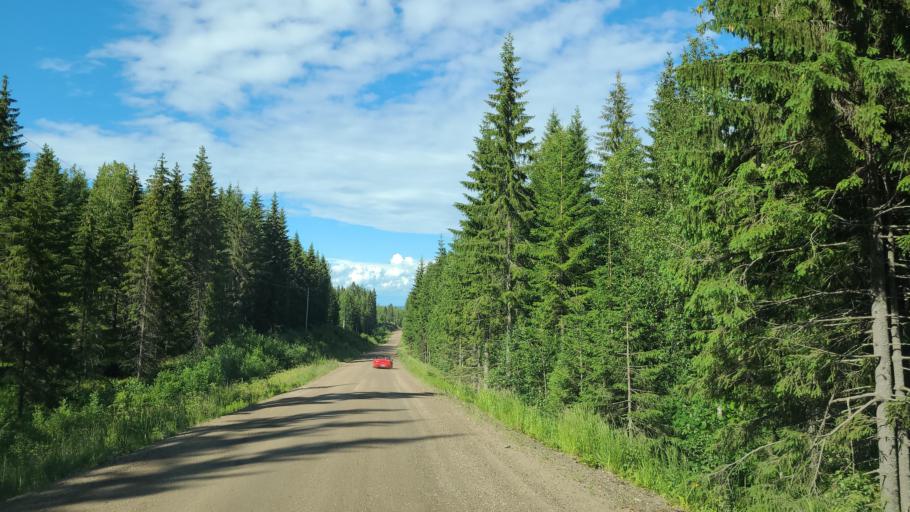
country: FI
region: Northern Savo
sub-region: Koillis-Savo
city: Kaavi
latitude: 62.9473
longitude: 28.7651
